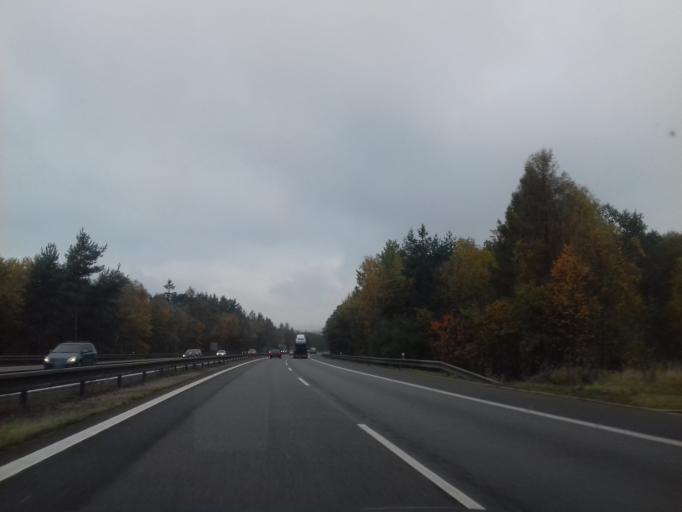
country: CZ
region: Vysocina
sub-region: Okres Pelhrimov
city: Zeliv
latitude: 49.5718
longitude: 15.2738
